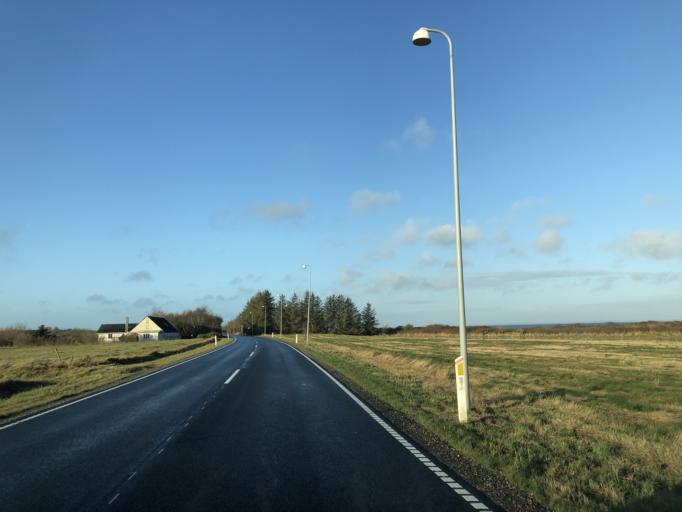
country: DK
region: Central Jutland
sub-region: Struer Kommune
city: Struer
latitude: 56.5528
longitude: 8.4818
